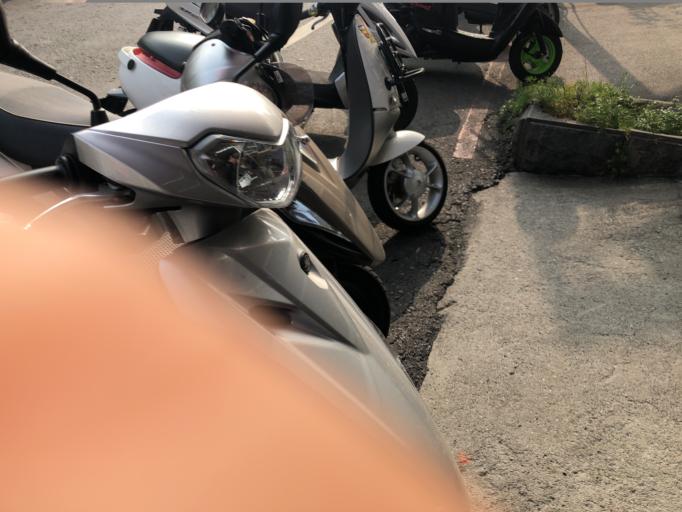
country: TW
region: Kaohsiung
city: Kaohsiung
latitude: 22.5967
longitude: 120.3340
